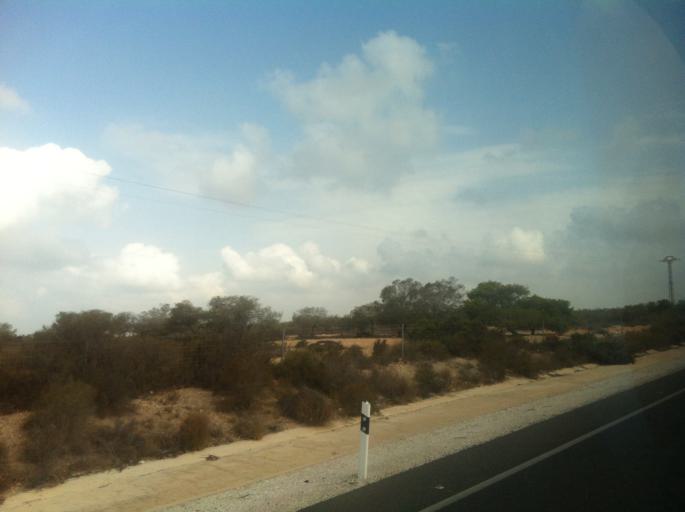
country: ES
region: Valencia
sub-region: Provincia de Alicante
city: Guardamar del Segura
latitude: 38.1344
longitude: -0.6584
